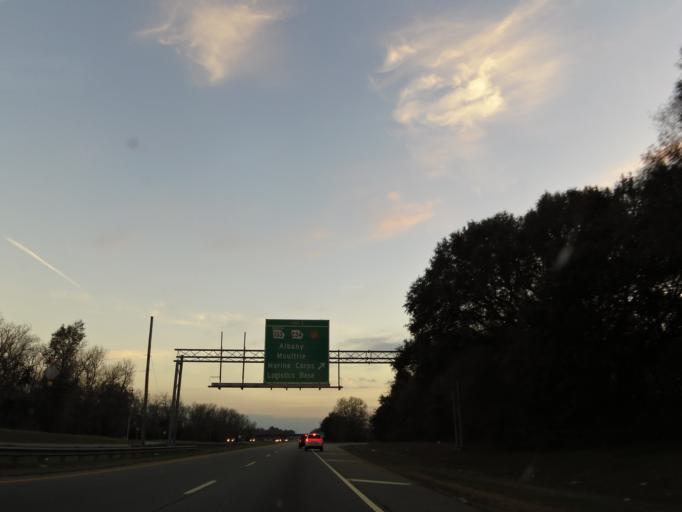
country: US
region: Georgia
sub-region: Dougherty County
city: Albany
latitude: 31.5510
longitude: -84.1152
